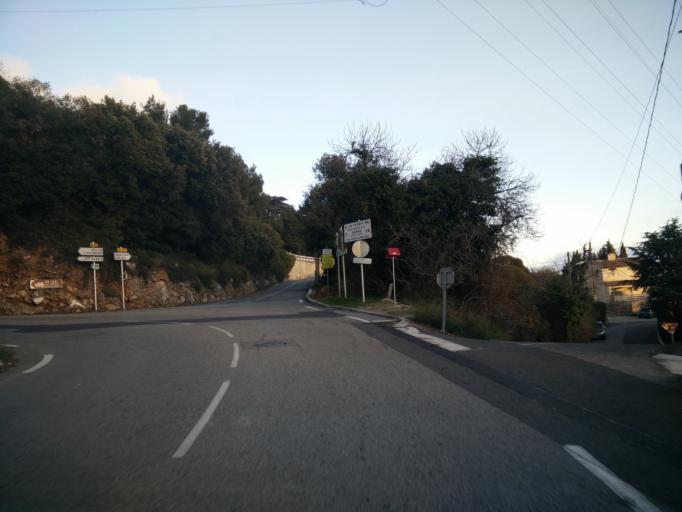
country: FR
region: Provence-Alpes-Cote d'Azur
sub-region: Departement des Alpes-Maritimes
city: La Turbie
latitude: 43.7531
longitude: 7.4071
